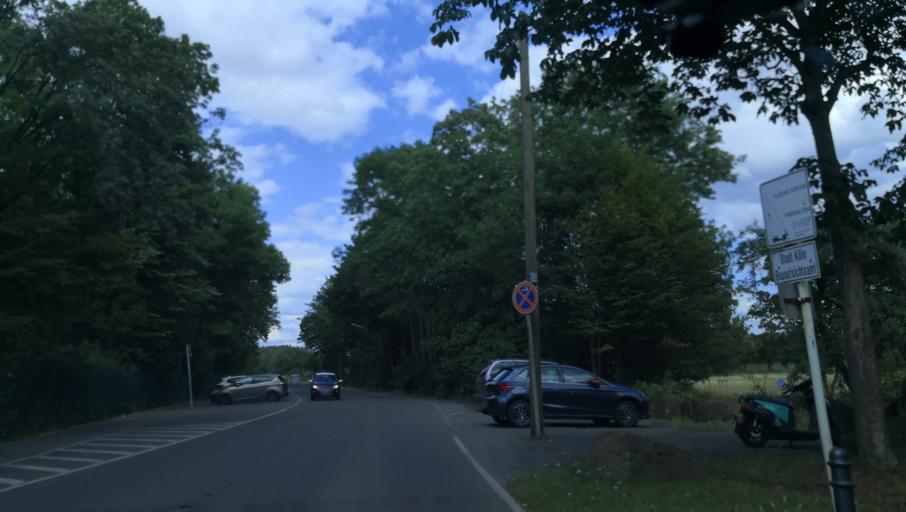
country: DE
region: North Rhine-Westphalia
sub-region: Regierungsbezirk Koln
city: Mengenich
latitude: 50.9705
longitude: 6.8856
